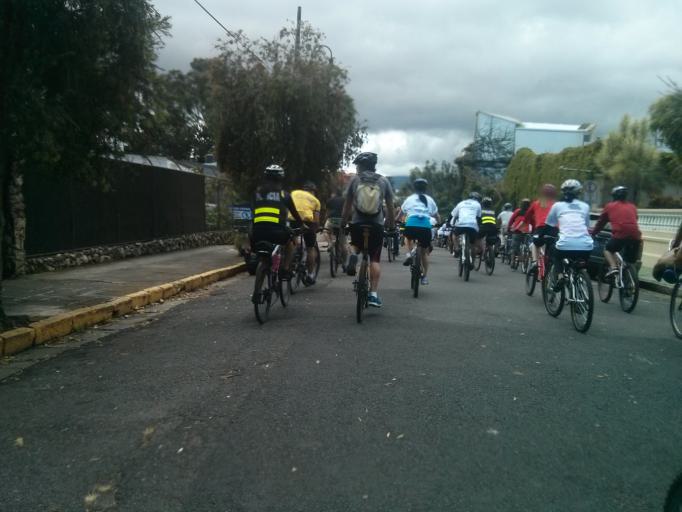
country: CR
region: San Jose
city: San Jose
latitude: 9.9379
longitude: -84.0723
